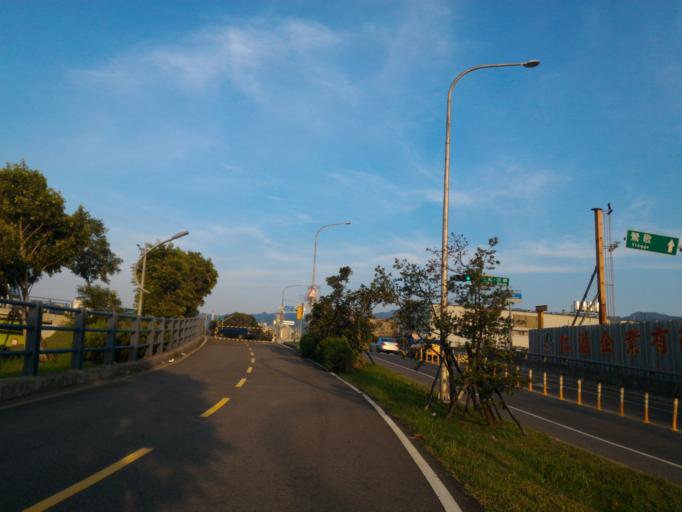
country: TW
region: Taipei
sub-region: Taipei
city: Banqiao
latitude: 24.9693
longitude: 121.4053
